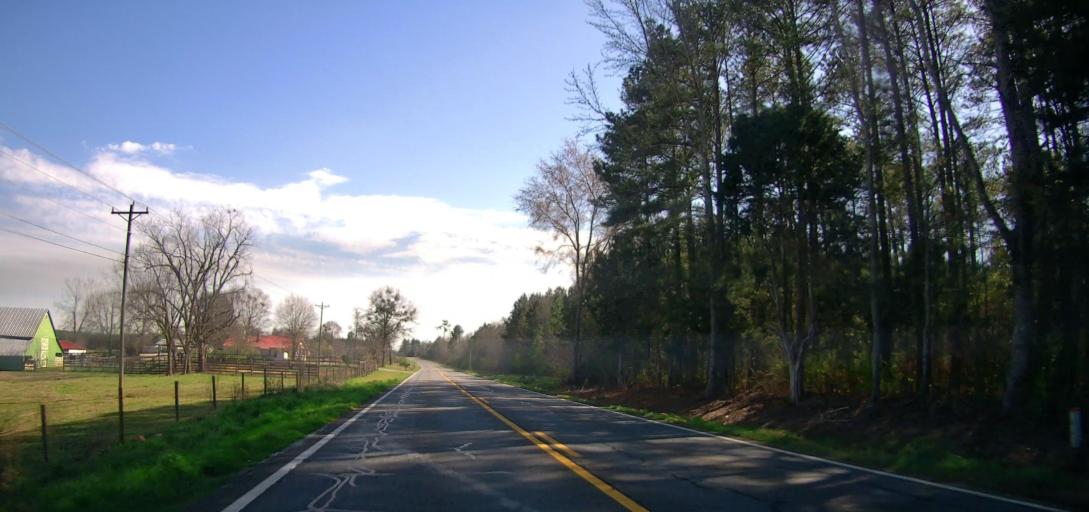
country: US
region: Georgia
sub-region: Butts County
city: Indian Springs
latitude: 33.1728
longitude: -83.9586
